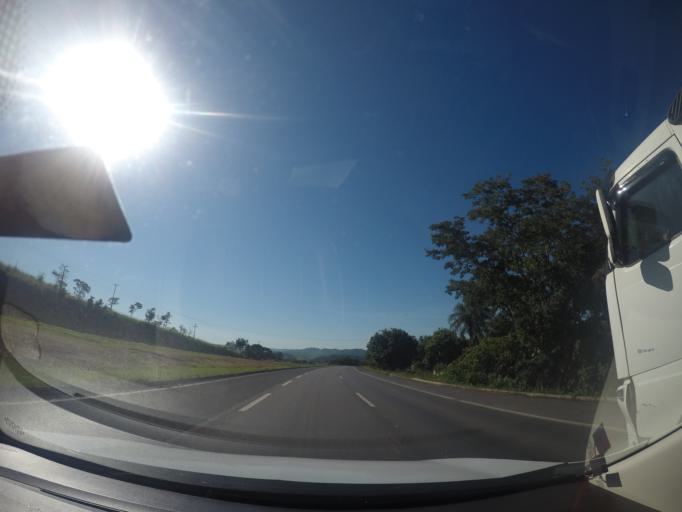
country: BR
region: Goias
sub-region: Piracanjuba
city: Piracanjuba
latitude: -17.3739
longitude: -49.2404
